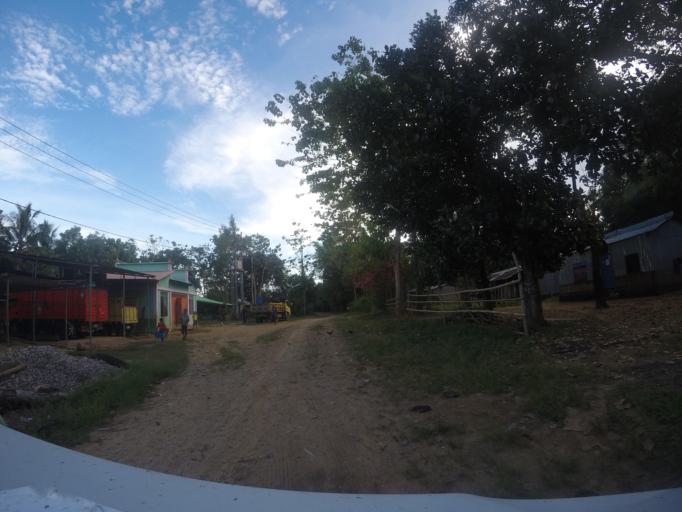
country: TL
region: Lautem
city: Lospalos
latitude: -8.5129
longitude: 126.9927
